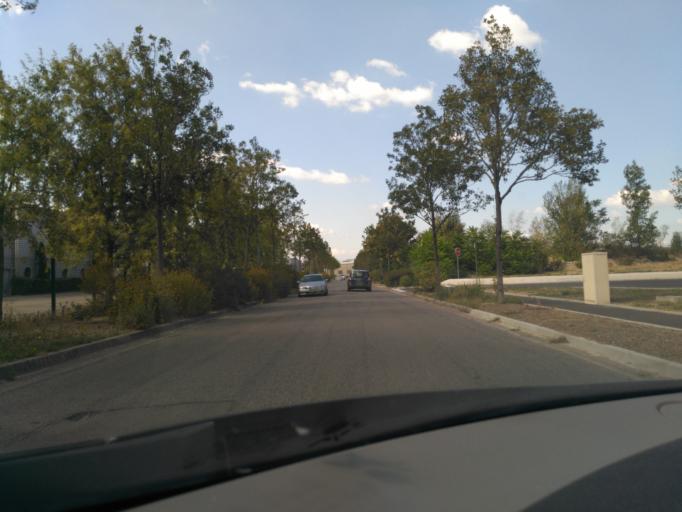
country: FR
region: Rhone-Alpes
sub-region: Departement du Rhone
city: Saint-Priest
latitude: 45.7128
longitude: 4.9619
